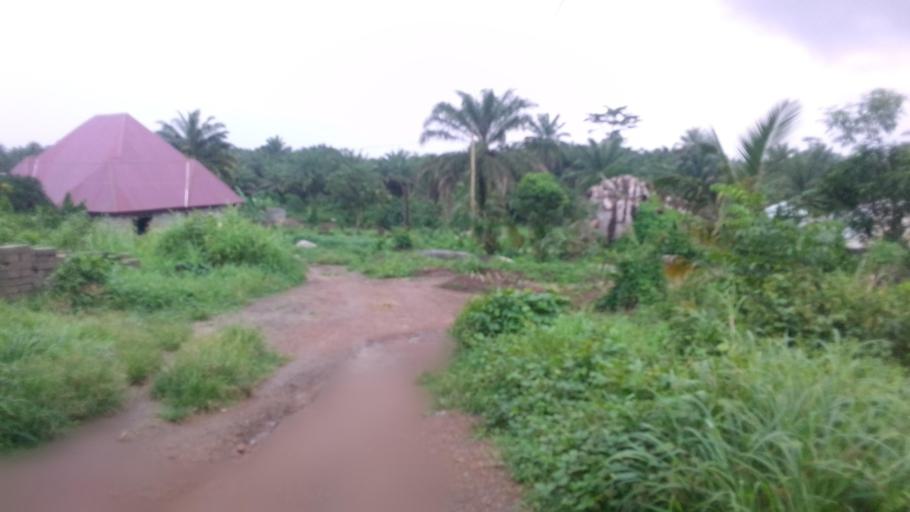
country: SL
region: Eastern Province
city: Kenema
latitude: 7.8841
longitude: -11.1621
